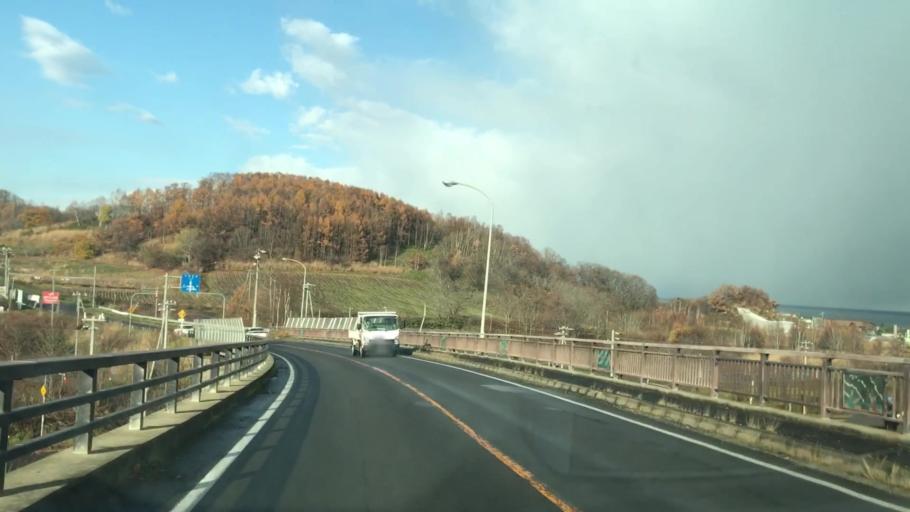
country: JP
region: Hokkaido
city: Yoichi
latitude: 43.1909
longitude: 140.8423
